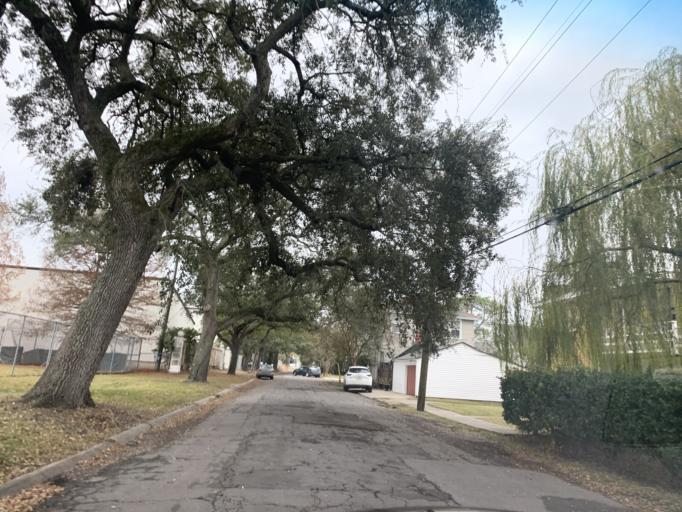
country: US
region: Louisiana
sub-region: Orleans Parish
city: New Orleans
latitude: 29.9868
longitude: -90.1072
